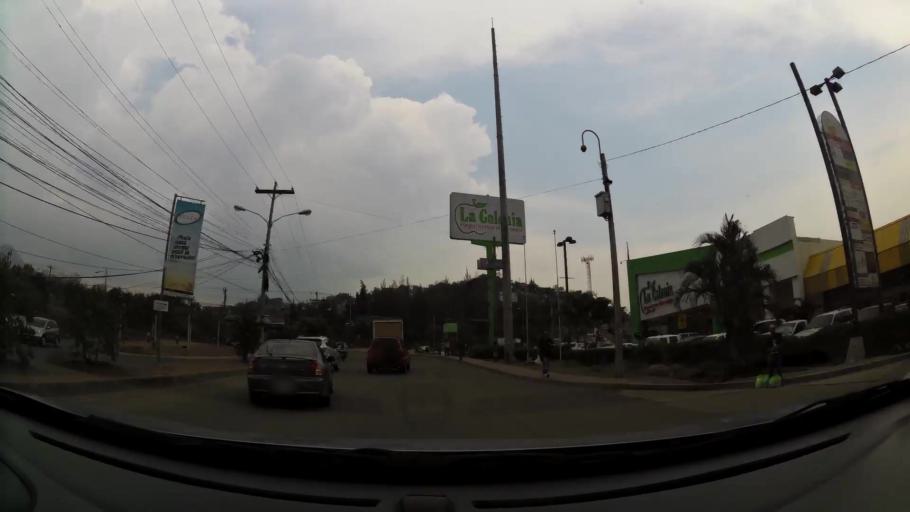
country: HN
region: Francisco Morazan
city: El Tablon
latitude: 14.0660
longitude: -87.1726
